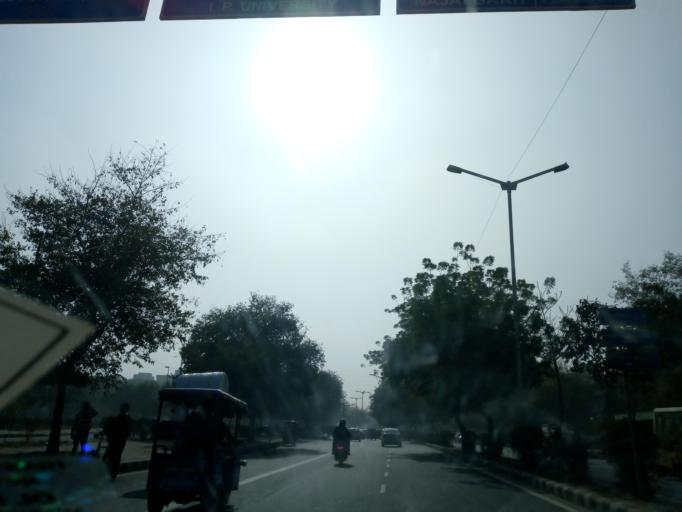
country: IN
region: NCT
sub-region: West Delhi
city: Nangloi Jat
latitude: 28.6027
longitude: 77.0431
